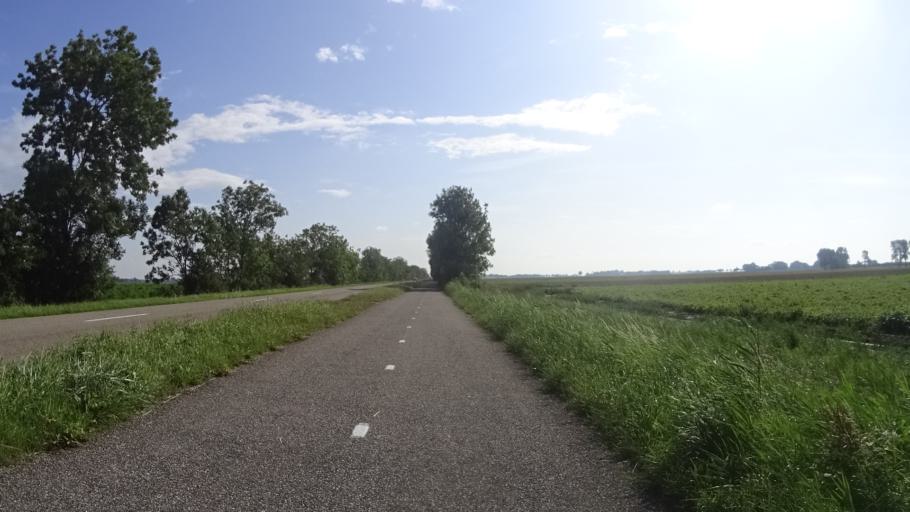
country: NL
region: Friesland
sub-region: Gemeente Franekeradeel
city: Franeker
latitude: 53.1885
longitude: 5.5634
